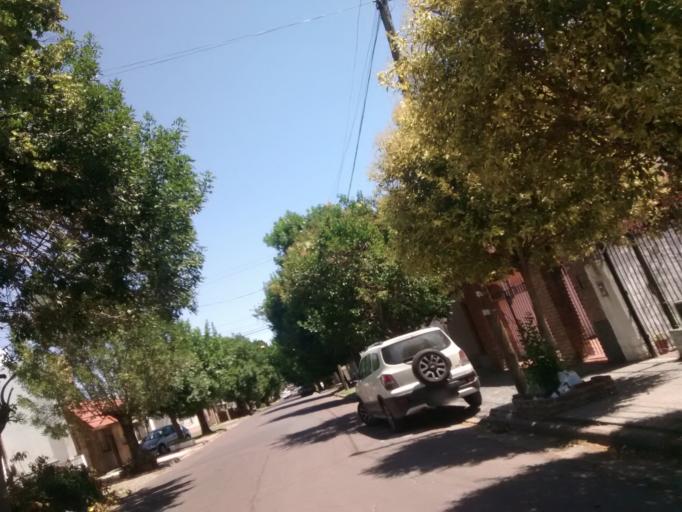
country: AR
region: Buenos Aires
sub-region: Partido de La Plata
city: La Plata
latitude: -34.9390
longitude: -57.9286
